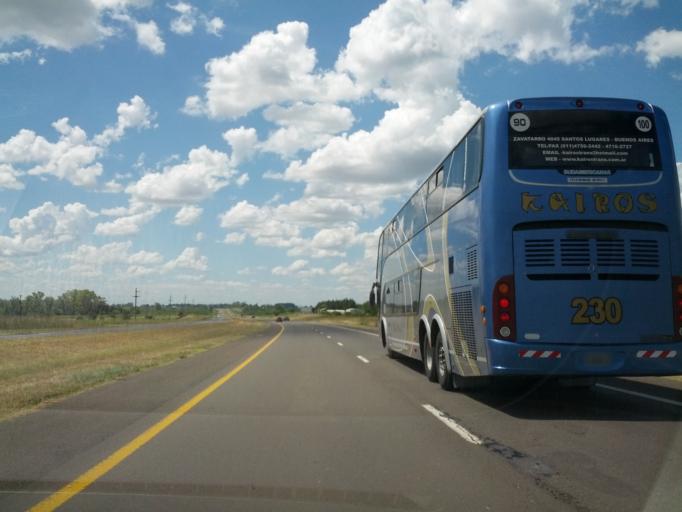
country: AR
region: Entre Rios
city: Concepcion del Uruguay
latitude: -32.4293
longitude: -58.2840
